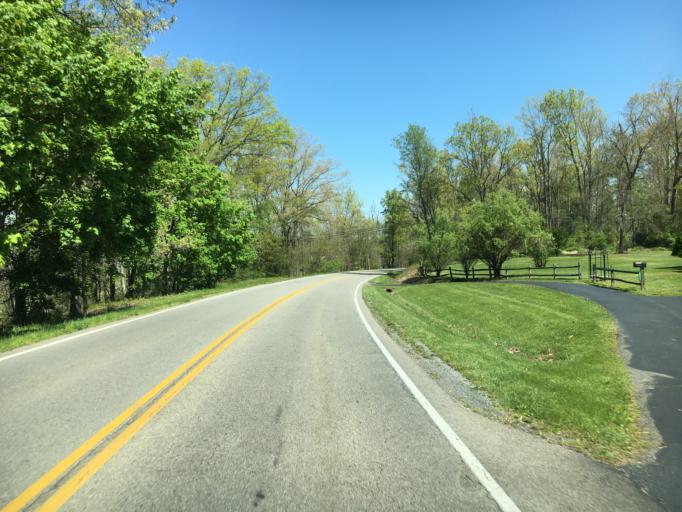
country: US
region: Virginia
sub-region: Augusta County
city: Crimora
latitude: 38.1647
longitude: -78.8505
